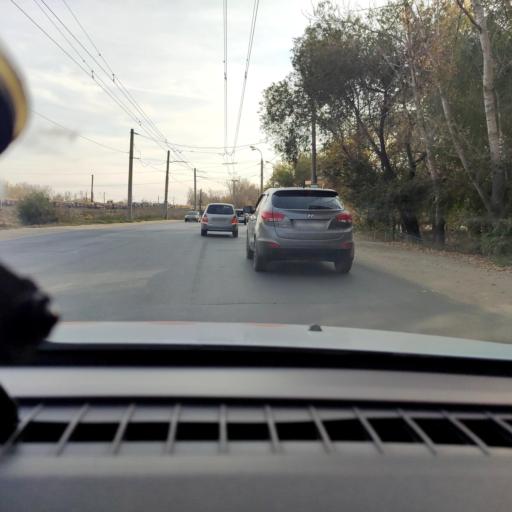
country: RU
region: Samara
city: Samara
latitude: 53.1552
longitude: 50.0919
